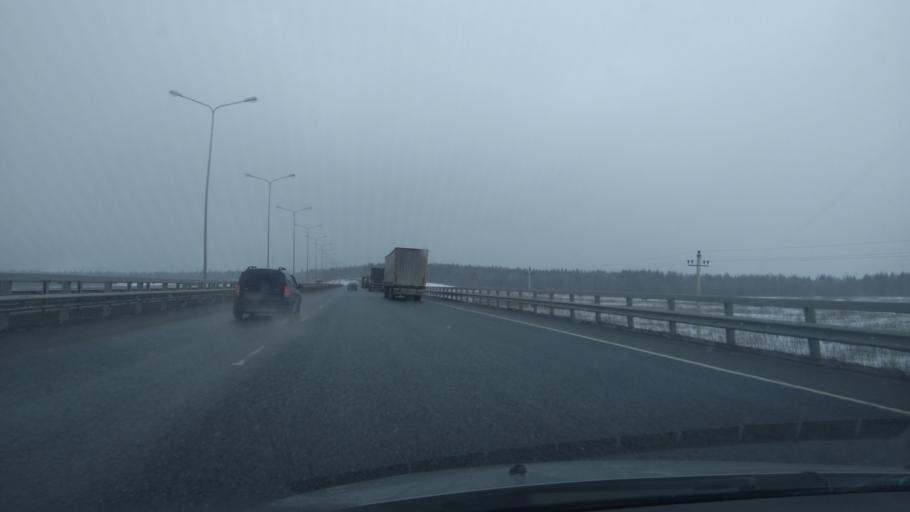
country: RU
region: Perm
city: Zvezdnyy
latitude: 57.7731
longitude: 56.3377
